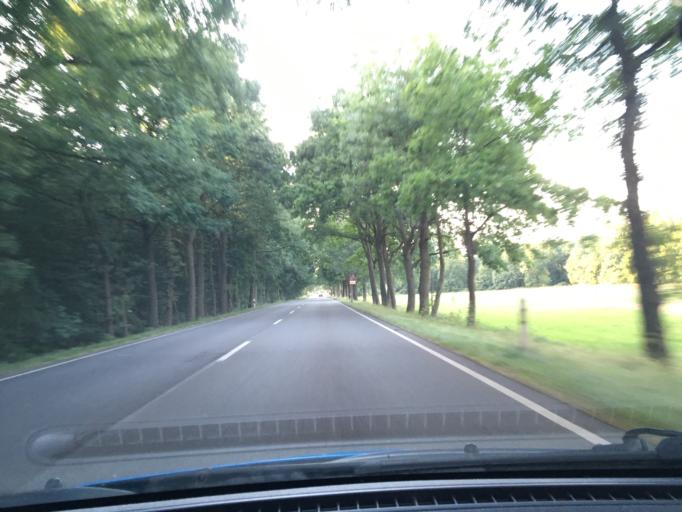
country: DE
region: Lower Saxony
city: Hambuhren
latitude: 52.6910
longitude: 9.9886
